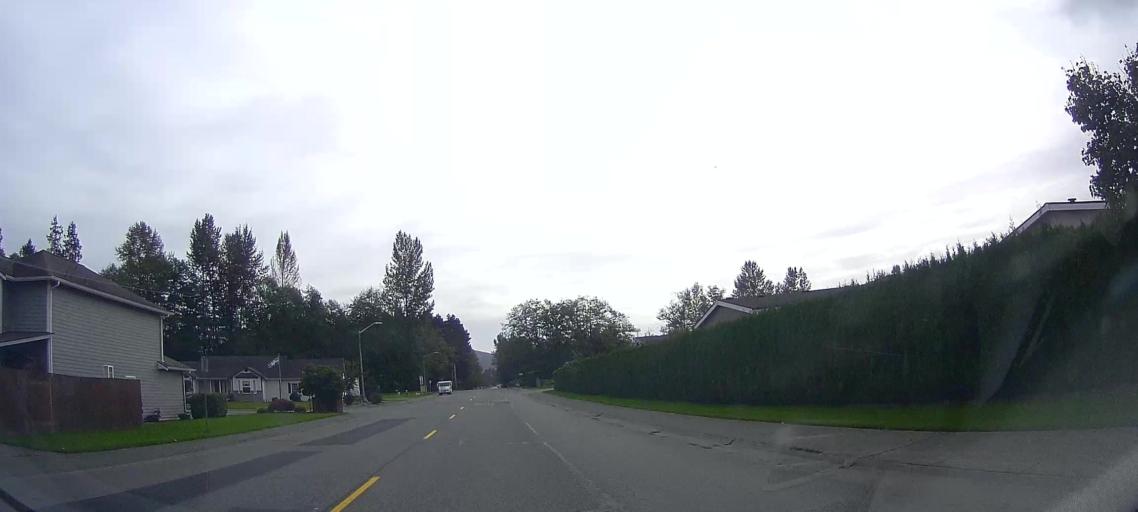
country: US
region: Washington
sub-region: Skagit County
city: Sedro-Woolley
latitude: 48.5182
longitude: -122.2341
